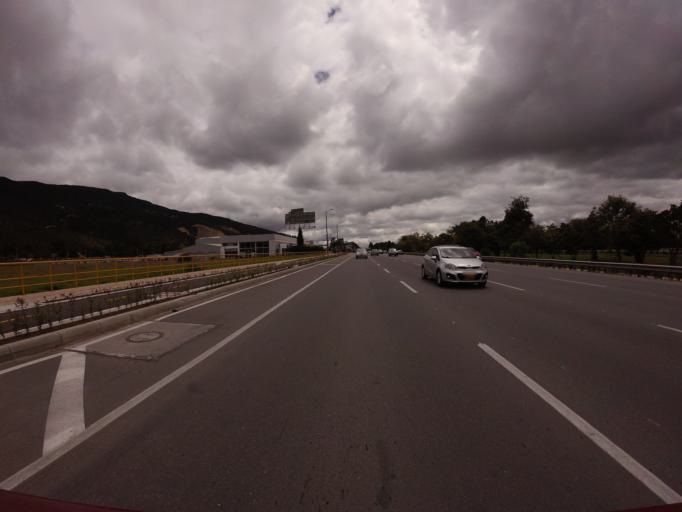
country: CO
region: Cundinamarca
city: Chia
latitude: 4.8454
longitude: -74.0306
